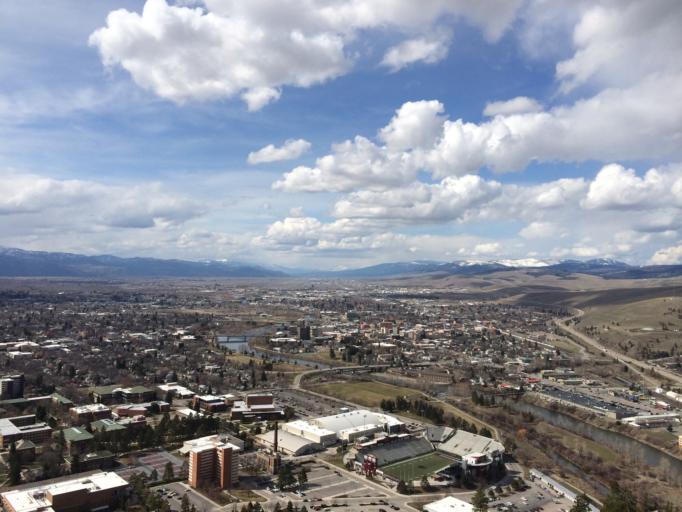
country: US
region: Montana
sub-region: Missoula County
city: Missoula
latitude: 46.8595
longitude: -113.9758
